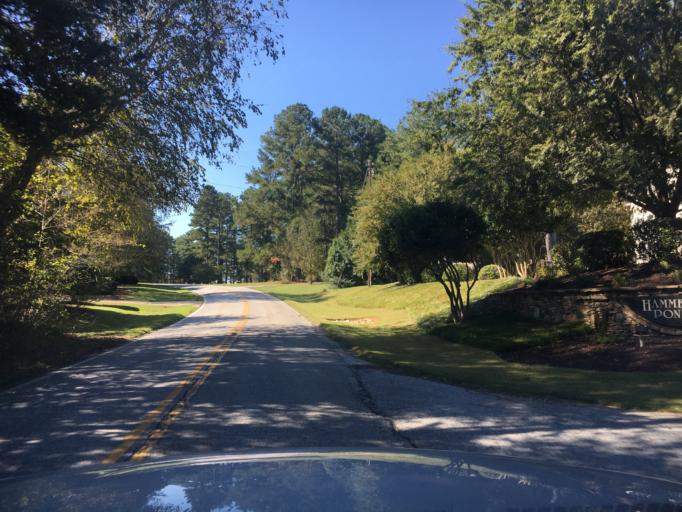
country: US
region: South Carolina
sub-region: Greenville County
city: Taylors
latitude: 34.8945
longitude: -82.2763
